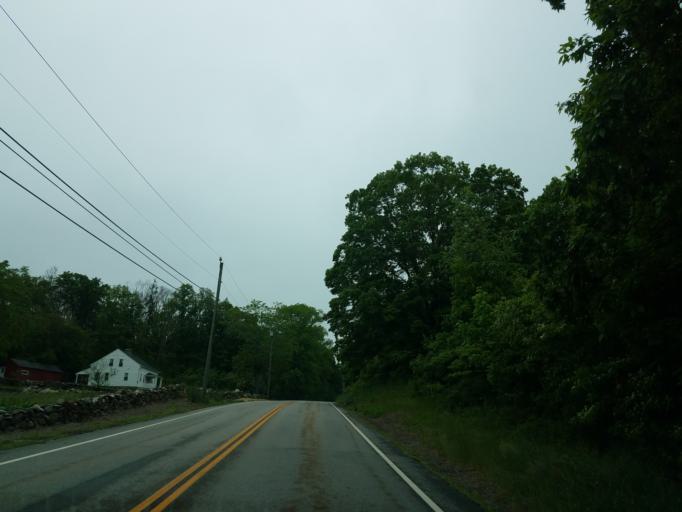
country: US
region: Connecticut
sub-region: Windham County
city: Plainfield Village
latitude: 41.7178
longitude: -71.9708
